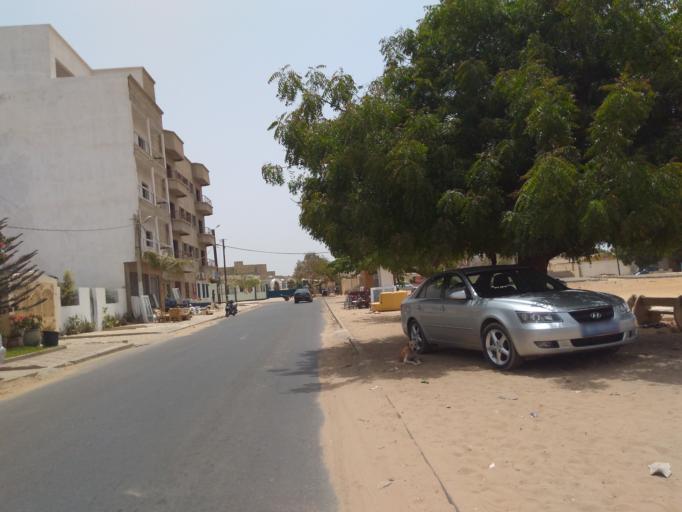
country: SN
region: Dakar
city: Grand Dakar
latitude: 14.7266
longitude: -17.4631
